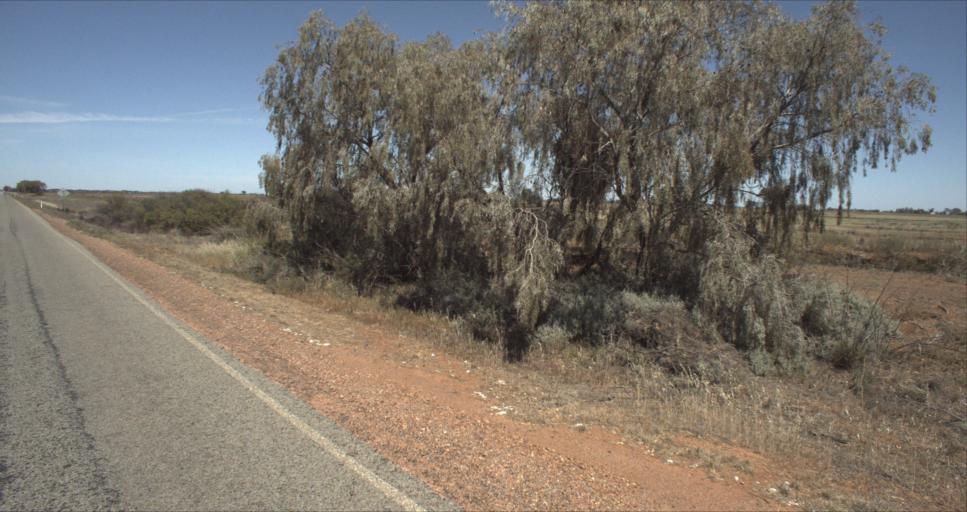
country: AU
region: New South Wales
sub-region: Leeton
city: Leeton
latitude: -34.4442
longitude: 146.2972
